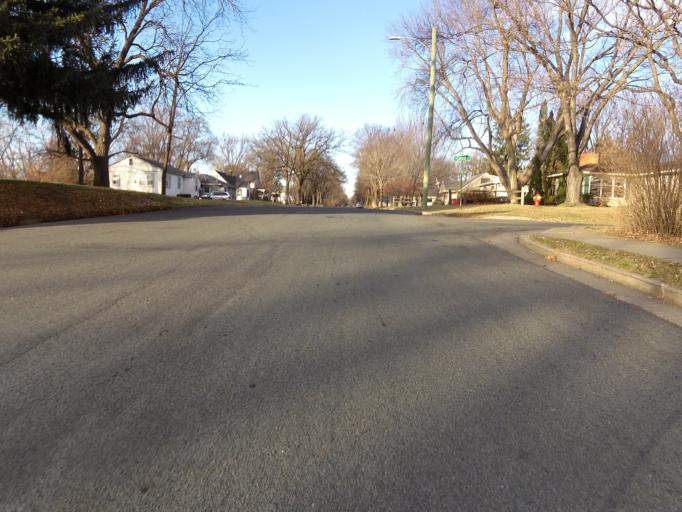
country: US
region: Wisconsin
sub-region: Pierce County
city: River Falls
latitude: 44.8566
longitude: -92.6336
